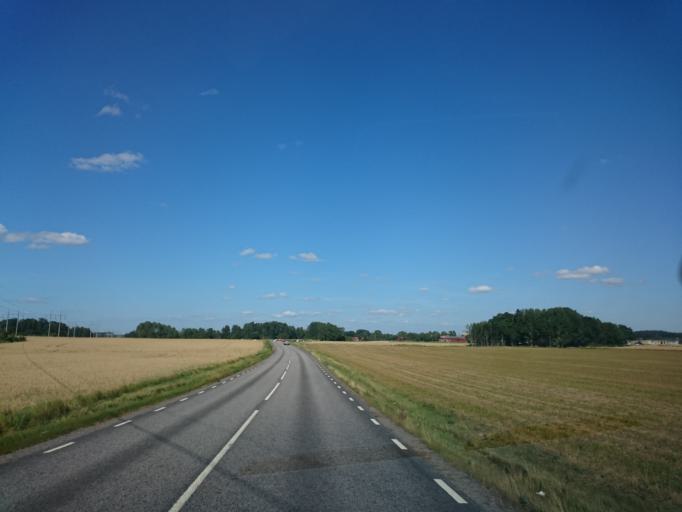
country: SE
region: OEstergoetland
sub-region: Linkopings Kommun
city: Linghem
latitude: 58.4221
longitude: 15.7681
